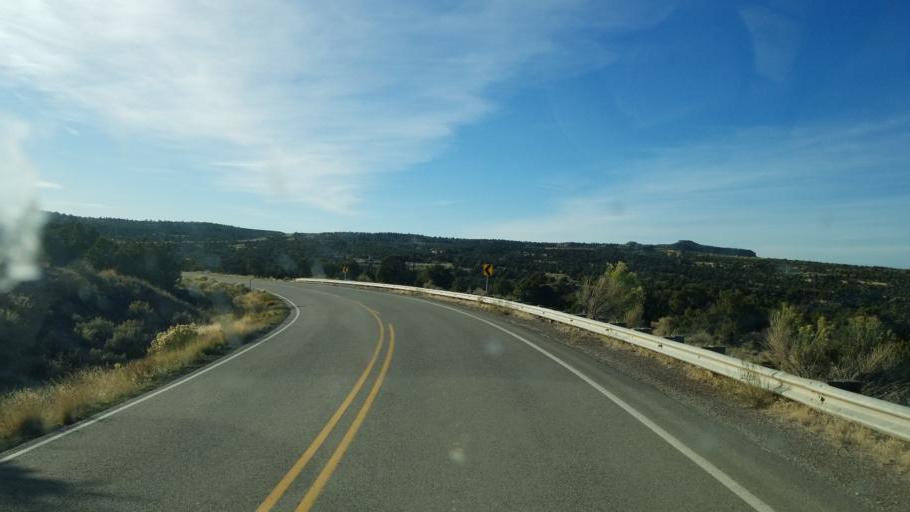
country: US
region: New Mexico
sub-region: San Juan County
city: Bloomfield
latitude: 36.7275
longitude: -107.6618
